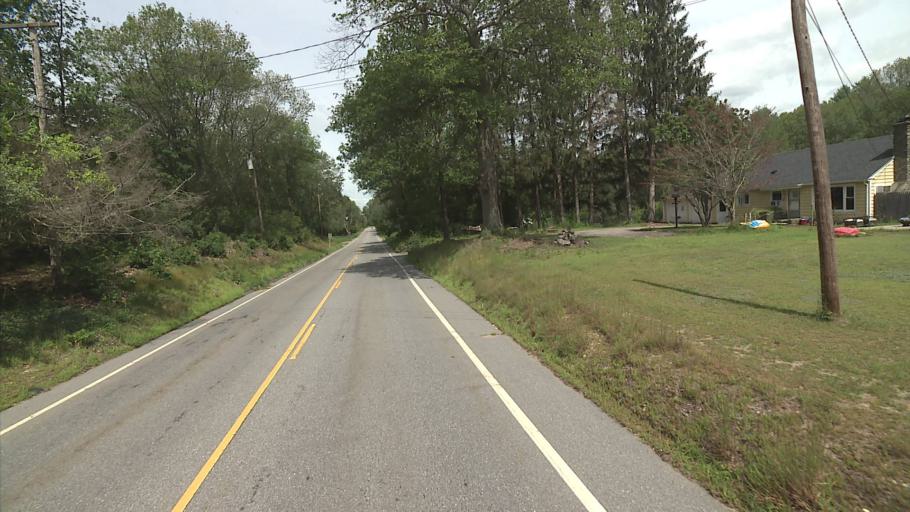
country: US
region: Connecticut
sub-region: Windham County
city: Putnam
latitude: 41.9085
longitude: -71.8677
